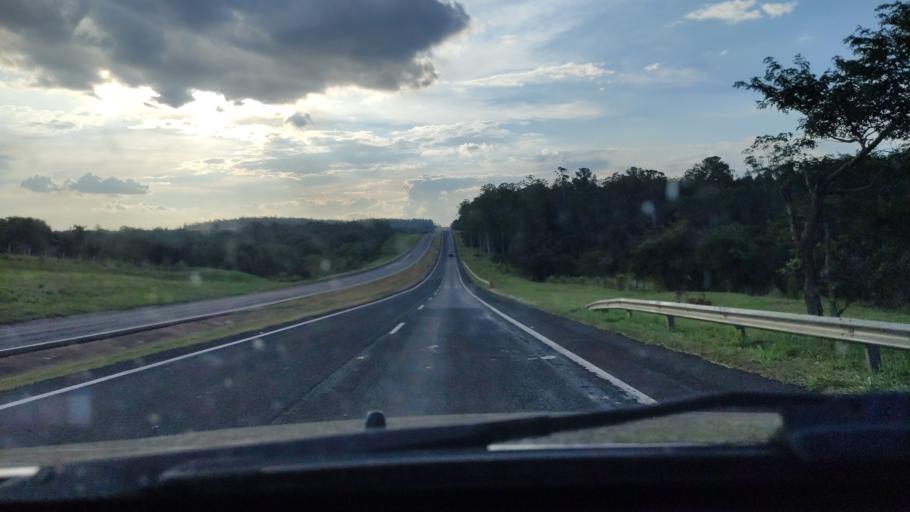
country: BR
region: Sao Paulo
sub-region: Rancharia
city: Rancharia
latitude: -22.4772
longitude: -50.9361
